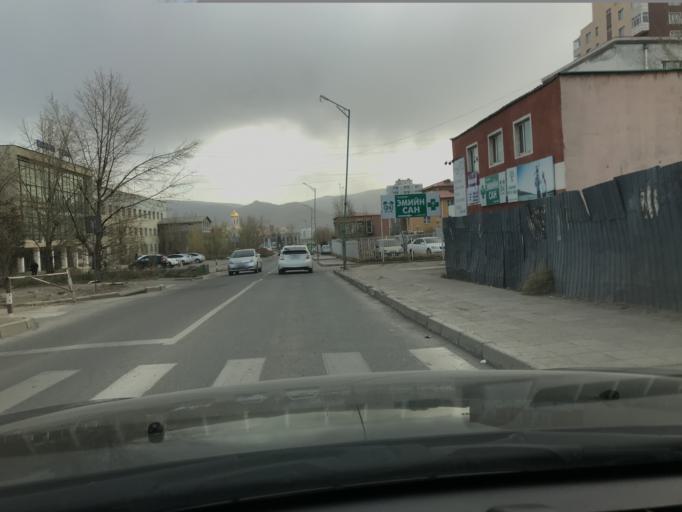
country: MN
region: Ulaanbaatar
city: Ulaanbaatar
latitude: 47.9193
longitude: 106.9591
